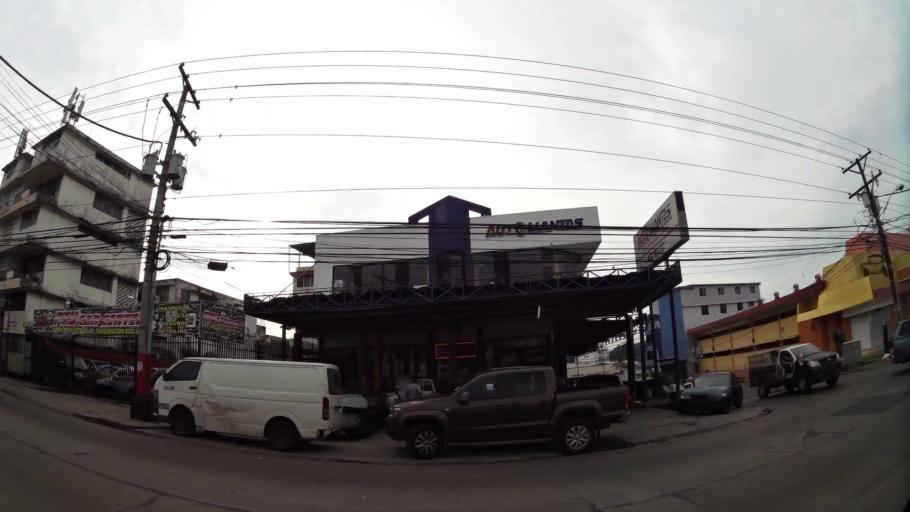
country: PA
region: Panama
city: Panama
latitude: 9.0046
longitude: -79.5202
